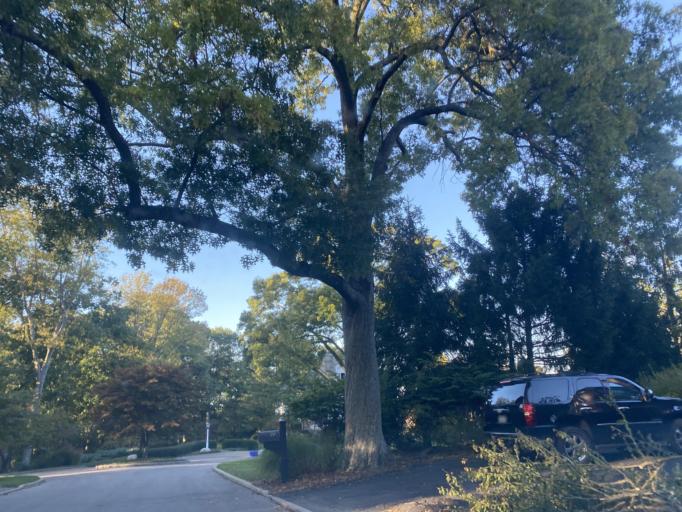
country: US
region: Kentucky
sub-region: Campbell County
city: Dayton
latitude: 39.1033
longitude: -84.4479
